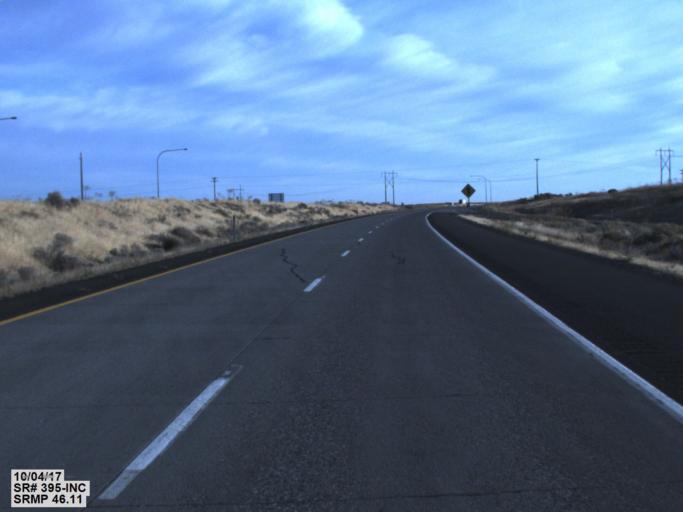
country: US
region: Washington
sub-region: Franklin County
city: Connell
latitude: 46.5695
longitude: -118.9898
